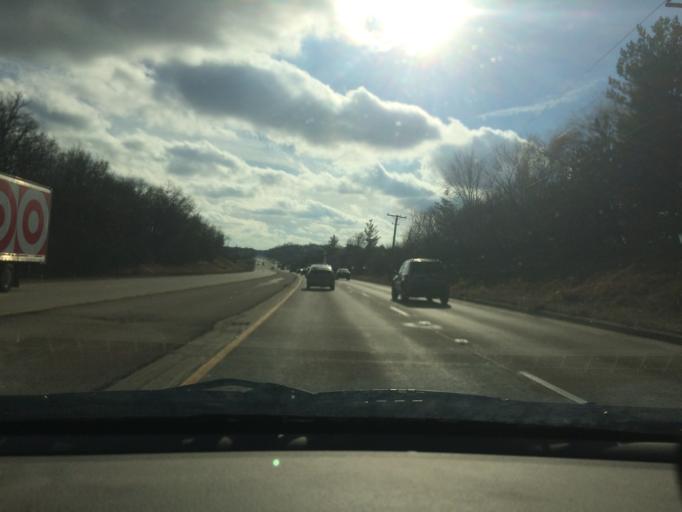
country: US
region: Illinois
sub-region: Cook County
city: Streamwood
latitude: 42.0284
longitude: -88.2028
